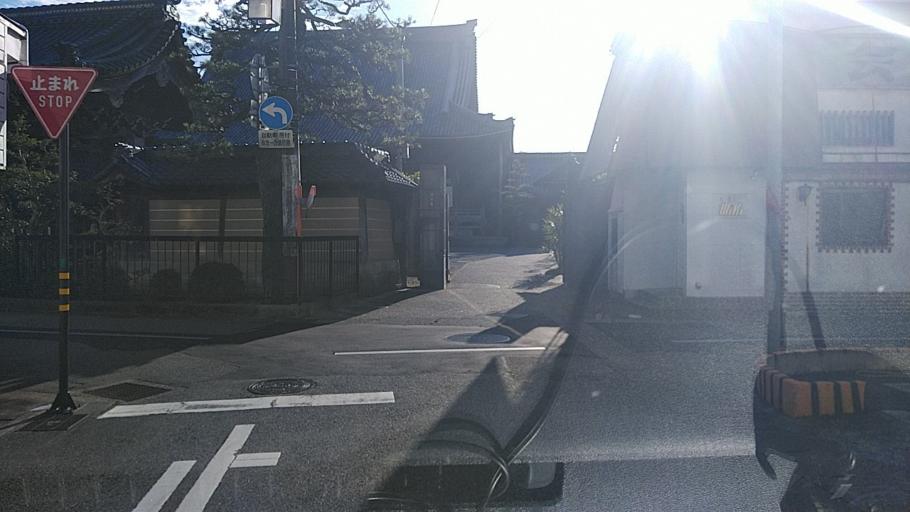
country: JP
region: Fukui
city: Maruoka
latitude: 36.3058
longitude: 136.3123
